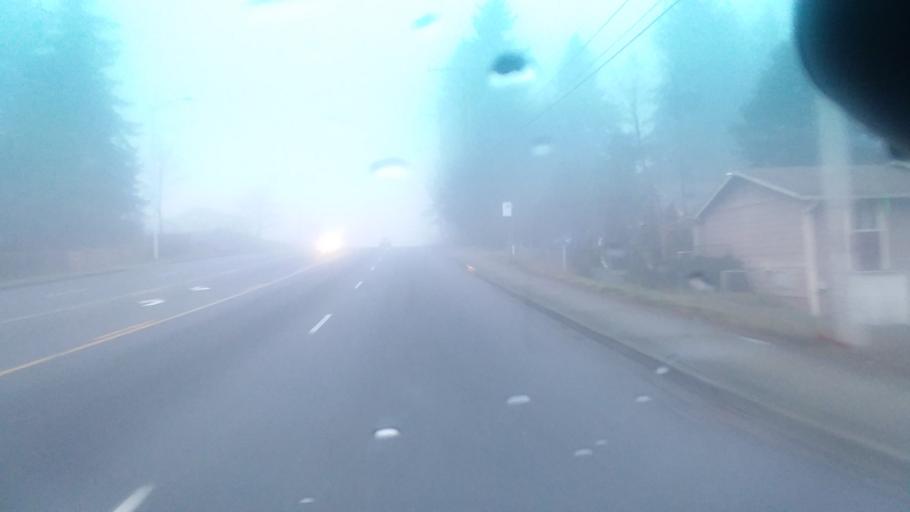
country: US
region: Washington
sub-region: Pierce County
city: Summit
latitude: 47.1550
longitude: -122.3188
